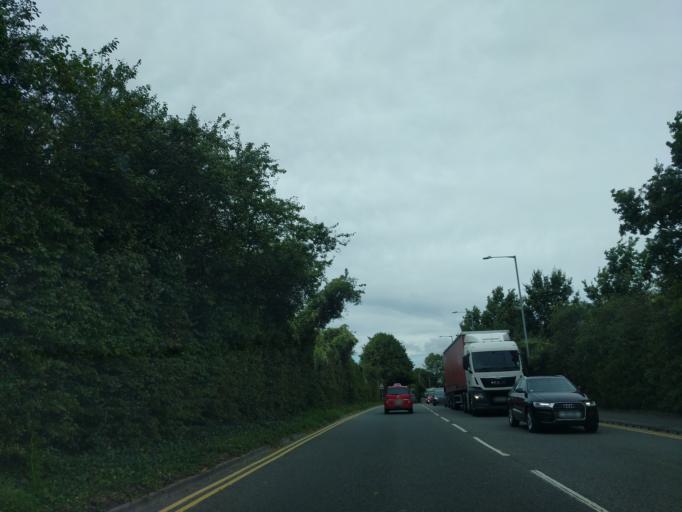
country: GB
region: England
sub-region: Lincolnshire
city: Grantham
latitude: 52.9128
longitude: -0.6476
